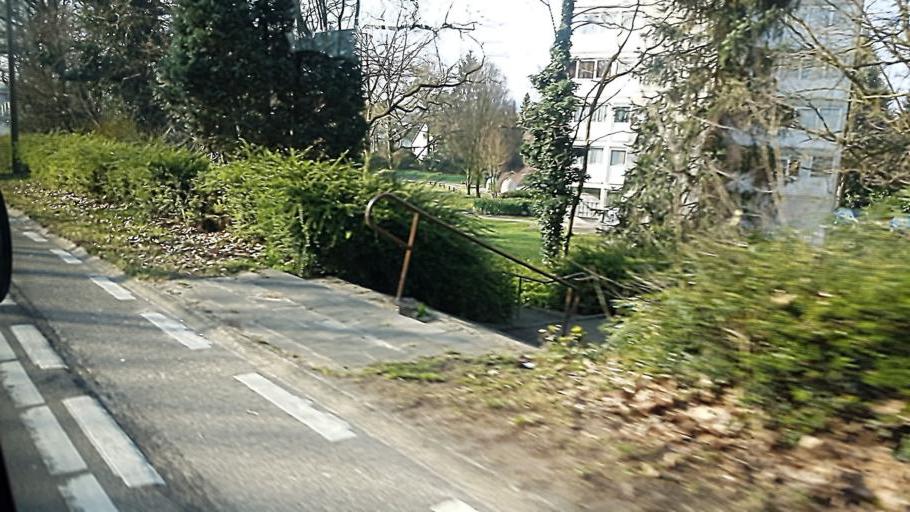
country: BE
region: Flanders
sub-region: Provincie Limburg
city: Genk
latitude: 51.0079
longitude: 5.4951
